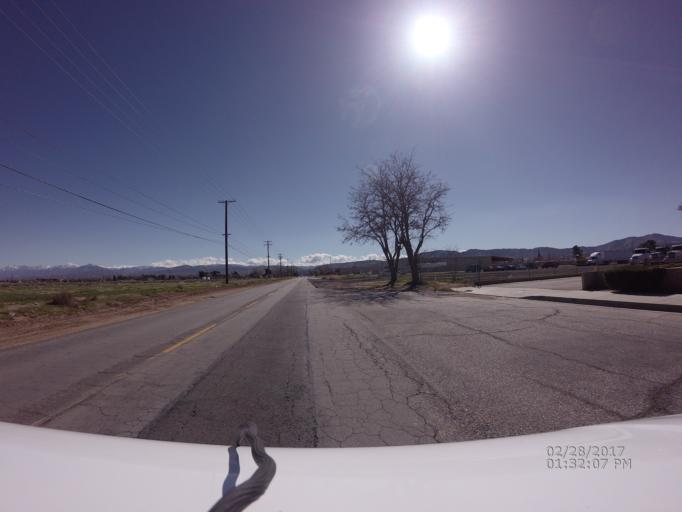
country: US
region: California
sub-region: Los Angeles County
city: Palmdale
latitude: 34.5919
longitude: -118.1120
